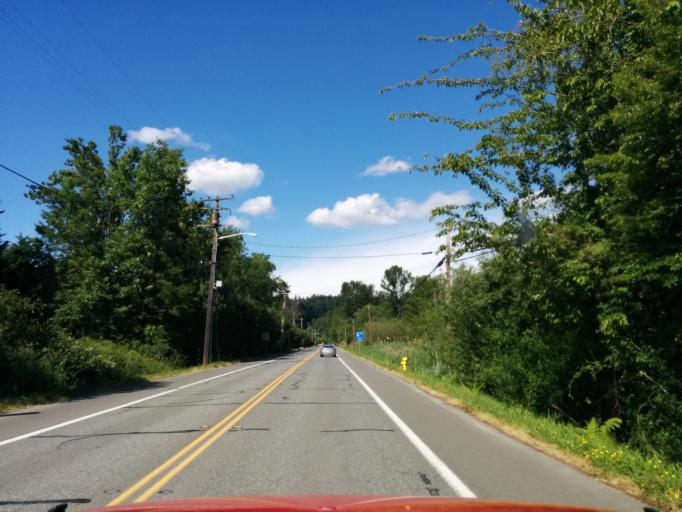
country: US
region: Washington
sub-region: King County
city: Sammamish
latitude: 47.6064
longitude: -122.0746
